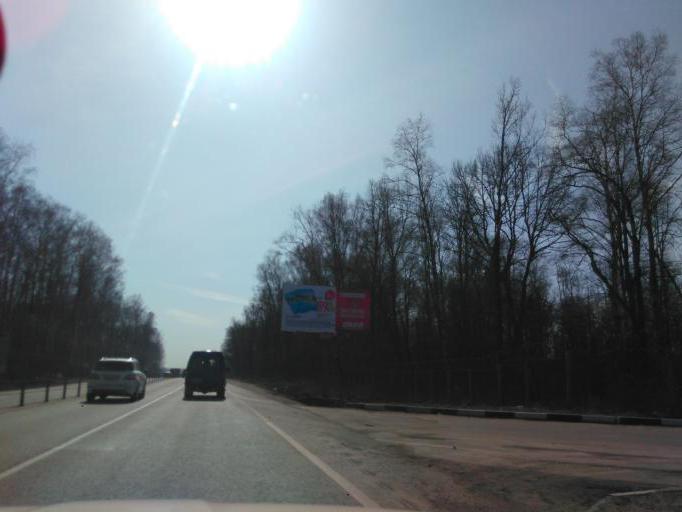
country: RU
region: Moskovskaya
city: Krasnogorsk
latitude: 55.8802
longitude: 37.3204
